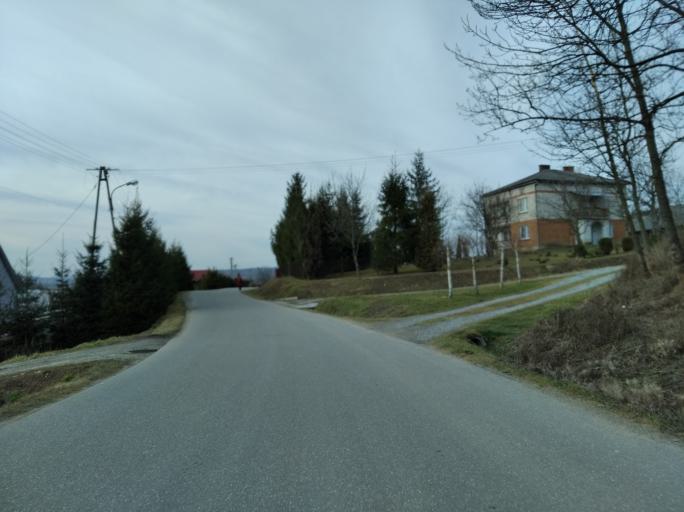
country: PL
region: Subcarpathian Voivodeship
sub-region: Powiat brzozowski
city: Gorki
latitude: 49.6497
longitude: 22.0353
